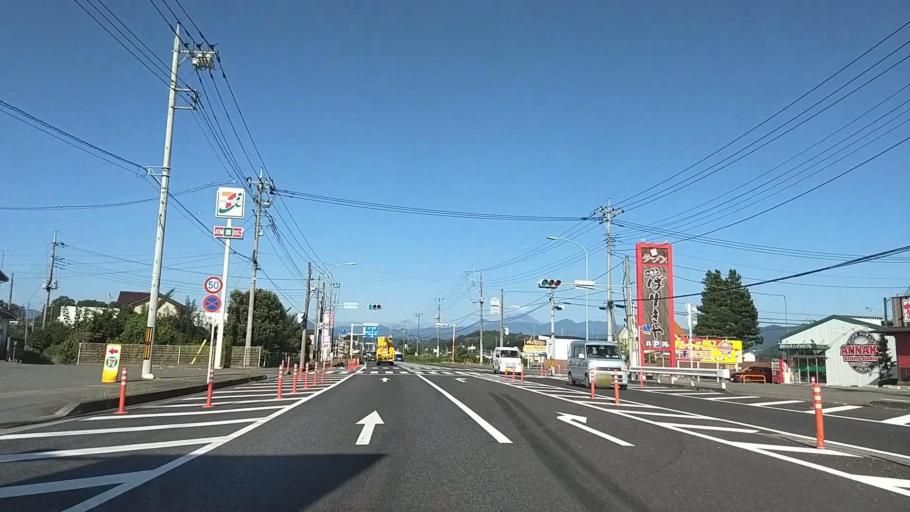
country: JP
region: Gunma
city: Annaka
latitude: 36.3335
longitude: 138.9059
